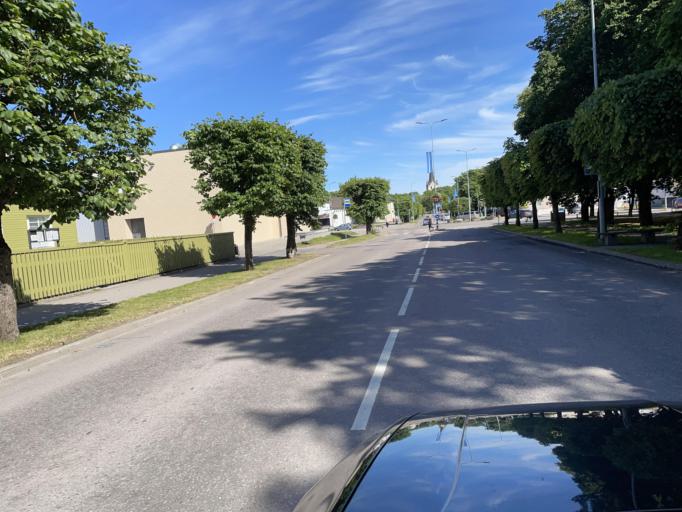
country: EE
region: Harju
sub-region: Keila linn
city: Keila
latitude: 59.3088
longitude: 24.4213
